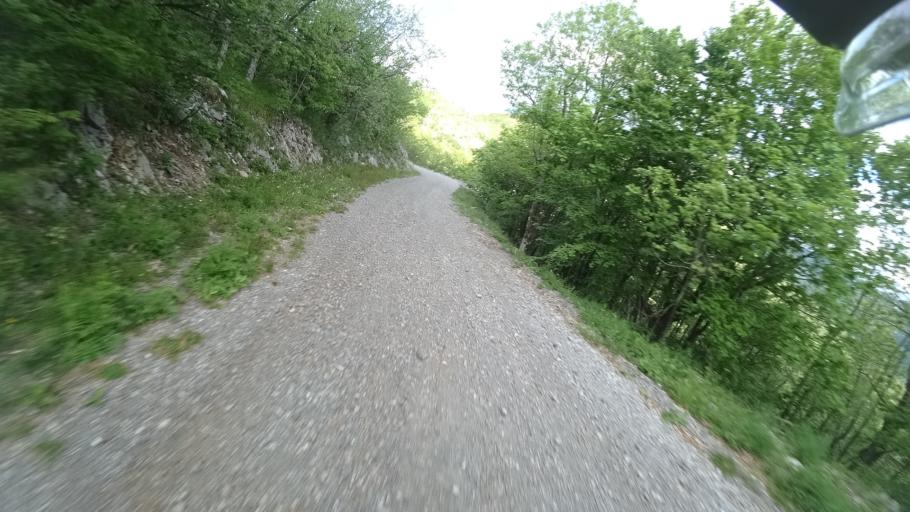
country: HR
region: Licko-Senjska
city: Gospic
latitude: 44.4560
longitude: 15.3001
